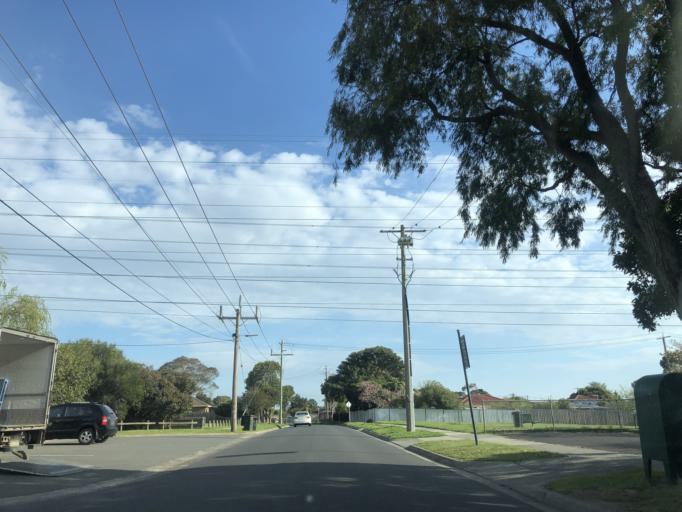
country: AU
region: Victoria
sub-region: Monash
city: Notting Hill
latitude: -37.8942
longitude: 145.1577
